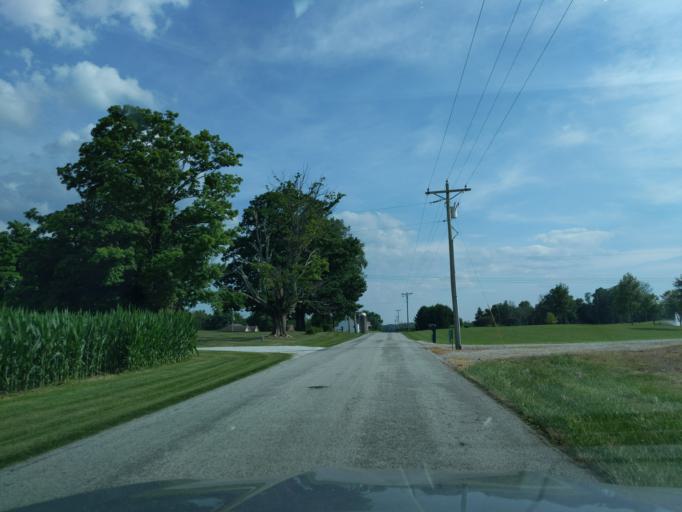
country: US
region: Indiana
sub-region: Decatur County
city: Greensburg
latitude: 39.2718
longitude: -85.4651
